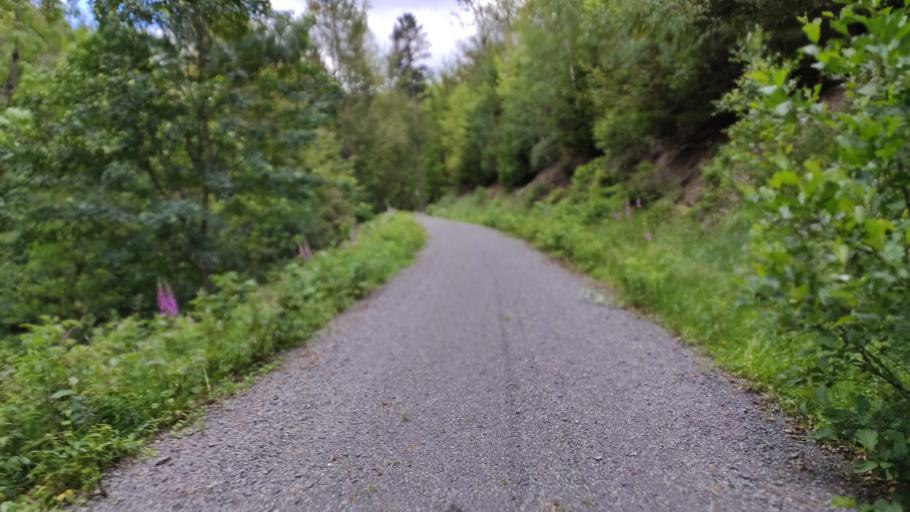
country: DE
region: Bavaria
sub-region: Upper Franconia
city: Tschirn
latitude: 50.3770
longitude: 11.4674
